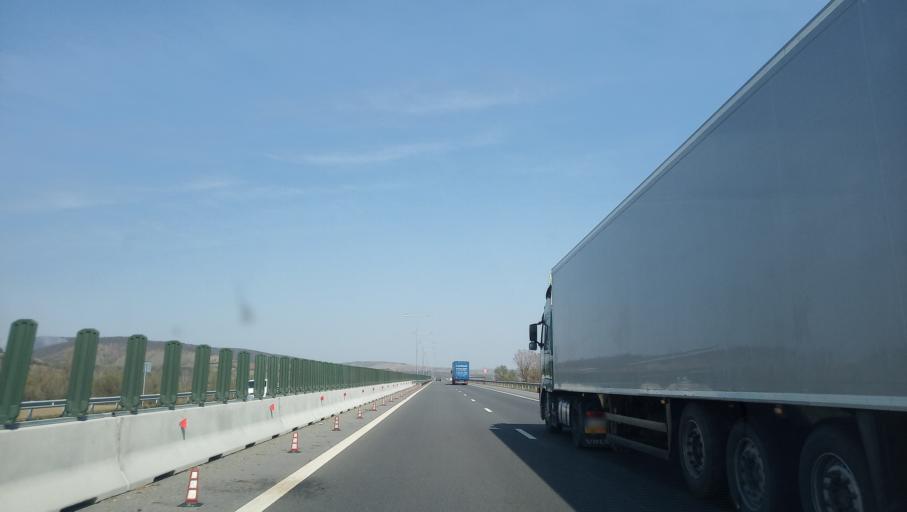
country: RO
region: Alba
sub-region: Comuna Miraslau
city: Miraslau
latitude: 46.3628
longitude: 23.7328
